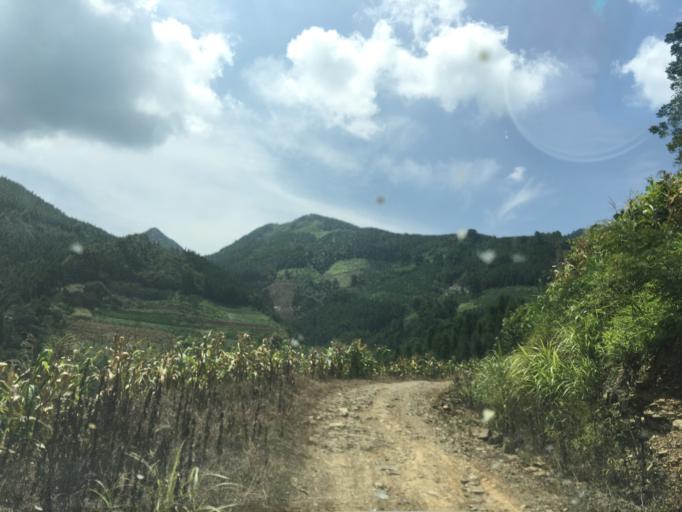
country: CN
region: Guangxi Zhuangzu Zizhiqu
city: Xinzhou
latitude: 24.9538
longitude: 105.7862
